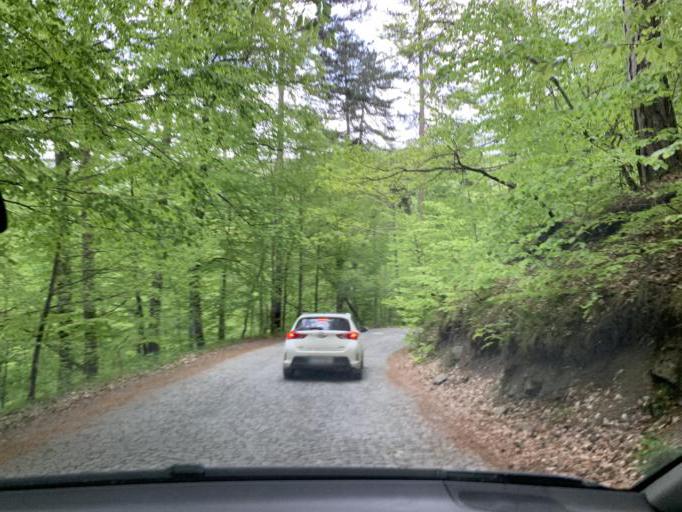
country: TR
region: Zonguldak
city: Egerci
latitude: 40.9405
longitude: 31.7445
